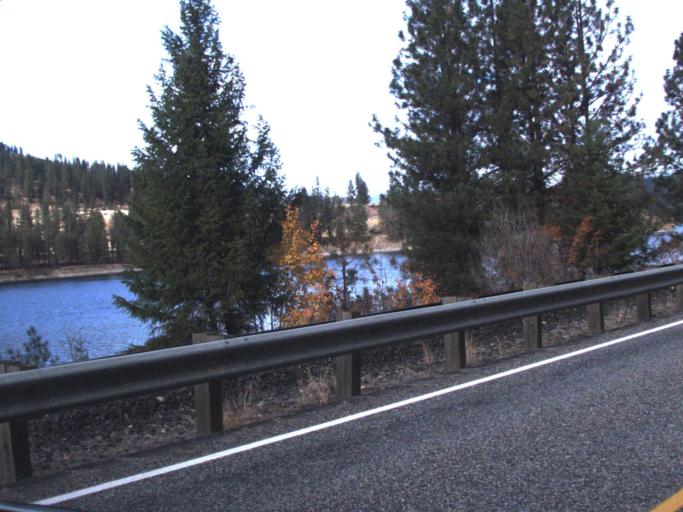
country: US
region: Washington
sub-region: Stevens County
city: Kettle Falls
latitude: 48.7691
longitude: -118.0247
